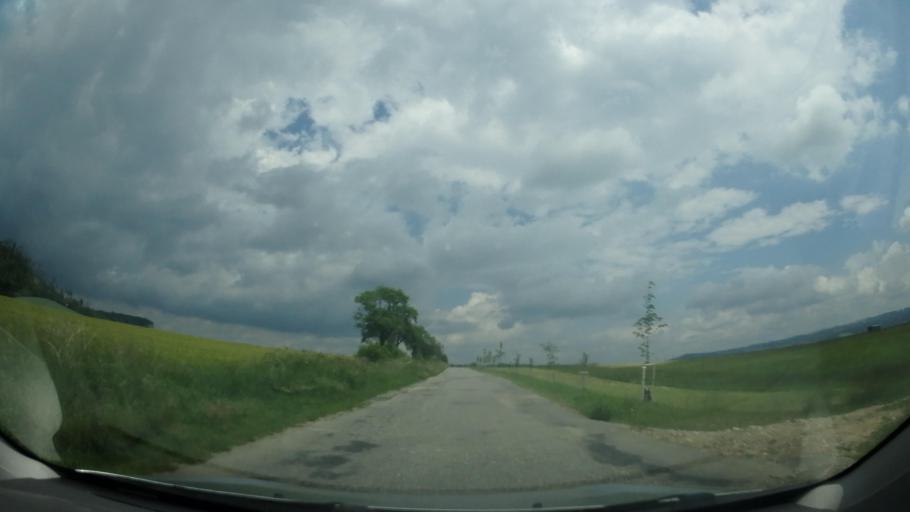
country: CZ
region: South Moravian
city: Boritov
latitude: 49.4376
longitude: 16.5961
